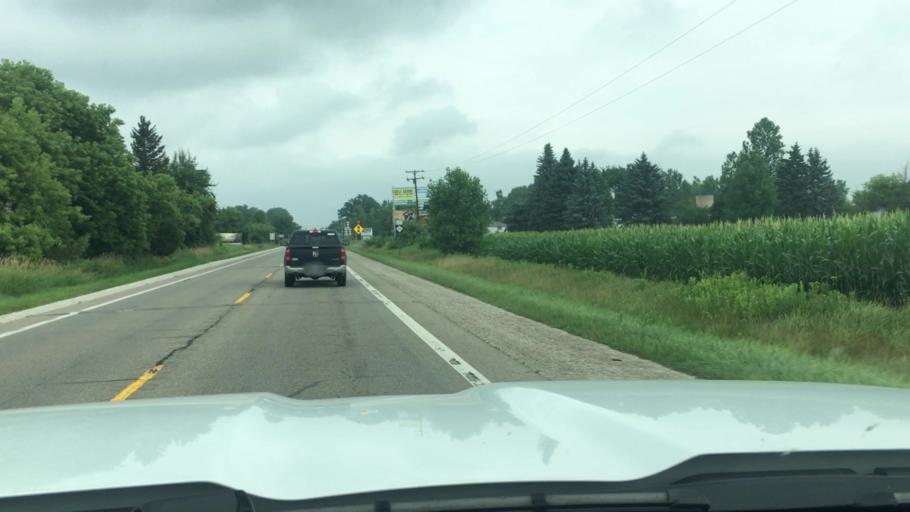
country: US
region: Michigan
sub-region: Sanilac County
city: Brown City
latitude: 43.2063
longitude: -83.0771
